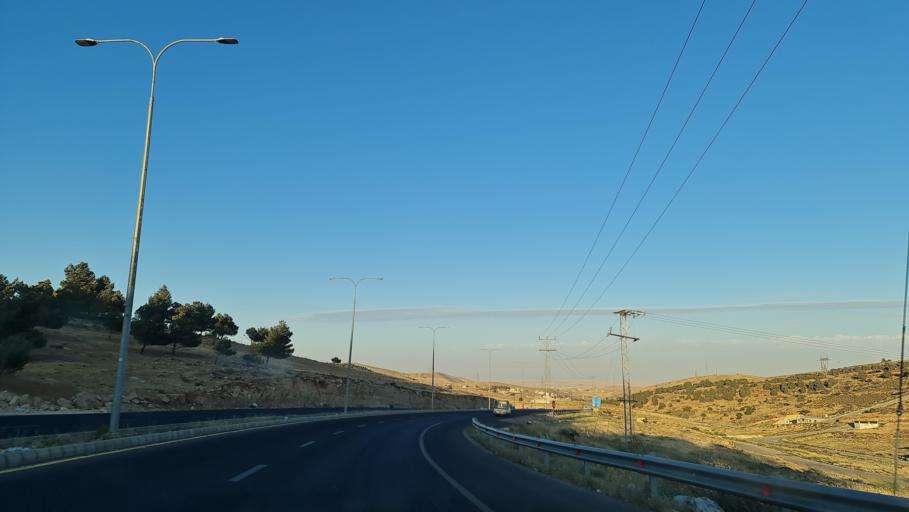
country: JO
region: Zarqa
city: Russeifa
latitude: 32.0926
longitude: 35.9681
